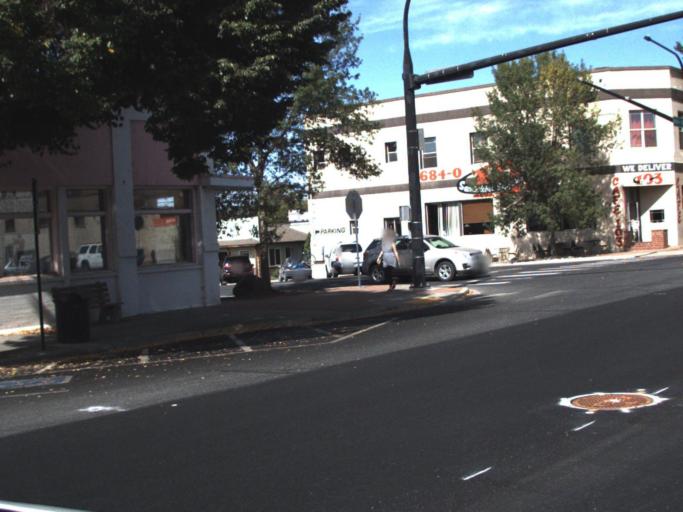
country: US
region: Washington
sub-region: Stevens County
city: Colville
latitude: 48.5443
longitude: -117.9058
